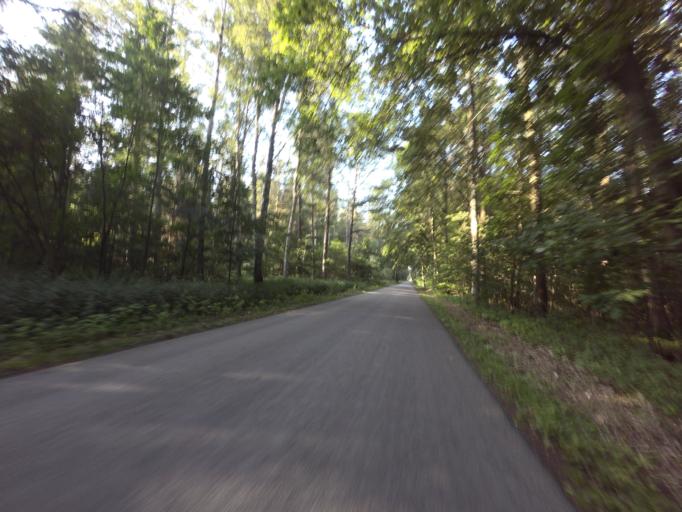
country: SE
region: Skane
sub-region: Landskrona
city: Asmundtorp
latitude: 55.8424
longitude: 12.9331
